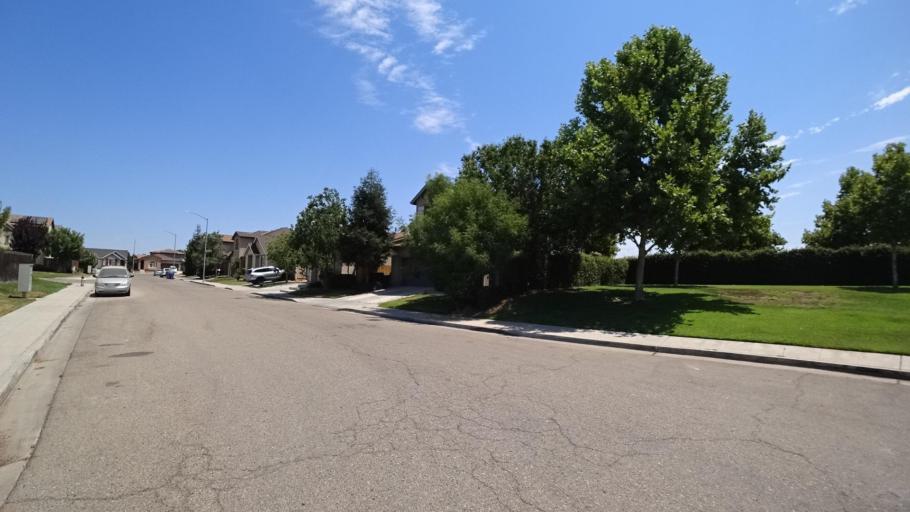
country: US
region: California
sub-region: Fresno County
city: Tarpey Village
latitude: 36.7854
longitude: -119.6554
